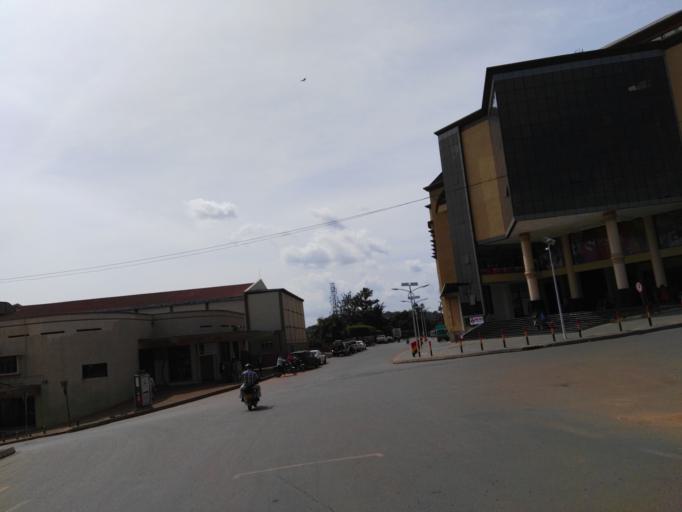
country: UG
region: Central Region
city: Kampala Central Division
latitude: 0.3185
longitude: 32.5755
